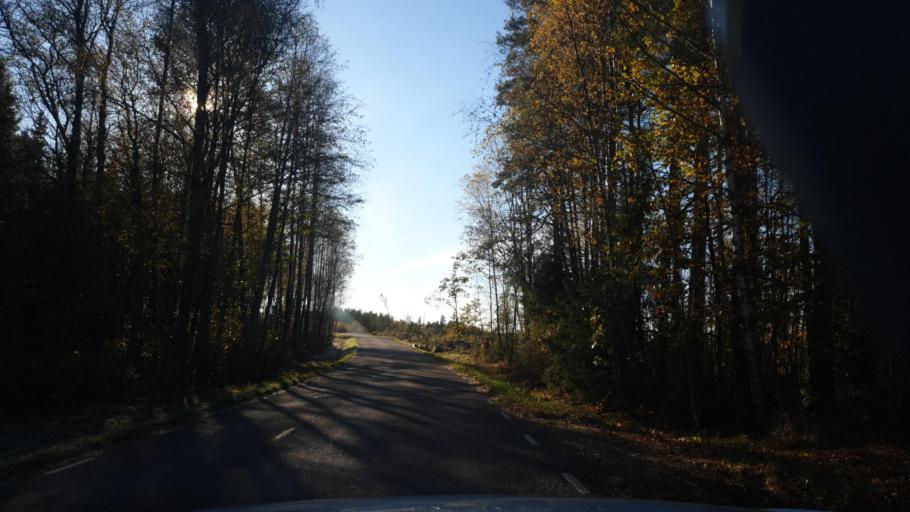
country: SE
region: Vaermland
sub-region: Grums Kommun
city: Grums
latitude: 59.4304
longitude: 13.0845
